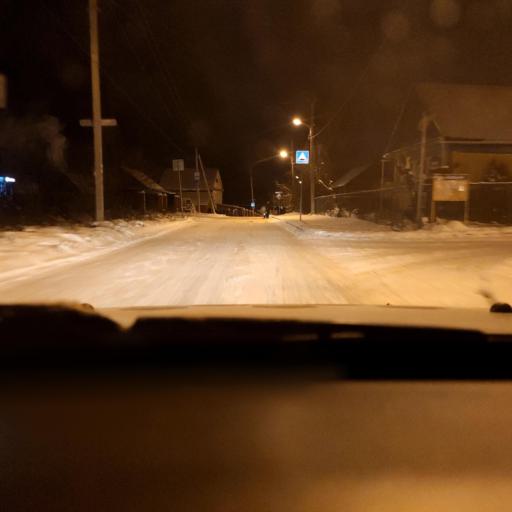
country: RU
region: Perm
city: Ferma
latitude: 57.9586
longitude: 56.3732
